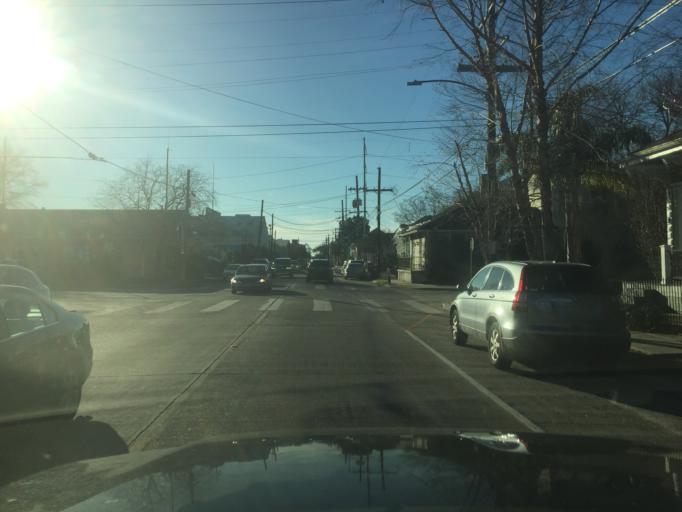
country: US
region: Louisiana
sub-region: Jefferson Parish
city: Marrero
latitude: 29.9175
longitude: -90.0973
